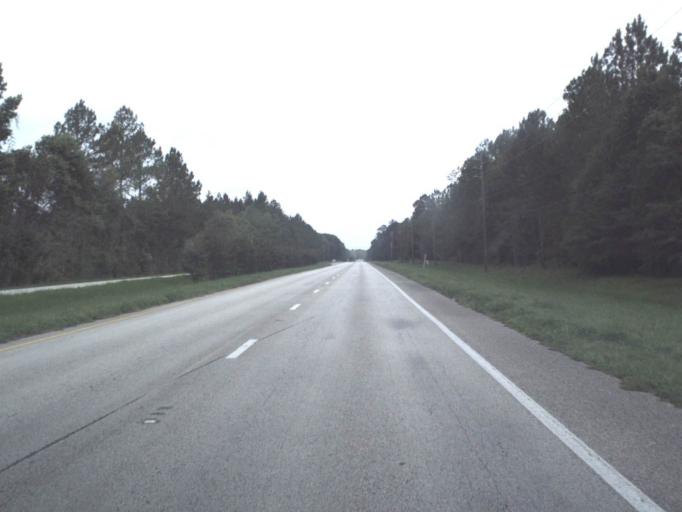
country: US
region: Florida
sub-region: Nassau County
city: Nassau Village-Ratliff
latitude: 30.4714
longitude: -81.7791
